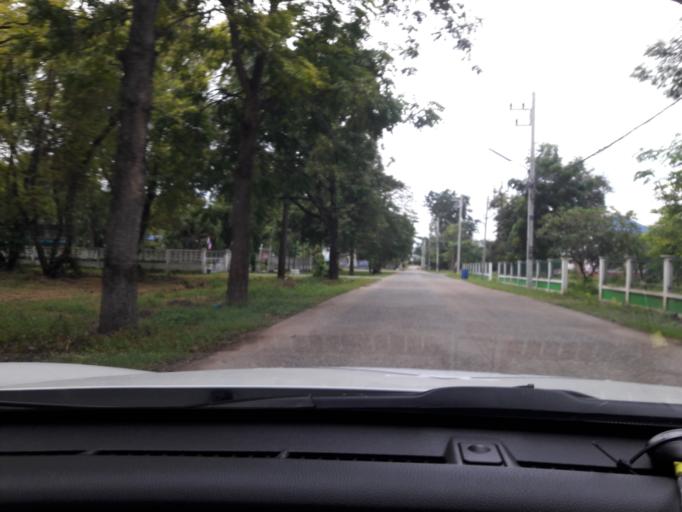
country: TH
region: Nakhon Sawan
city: Tak Fa
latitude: 15.3508
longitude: 100.4952
